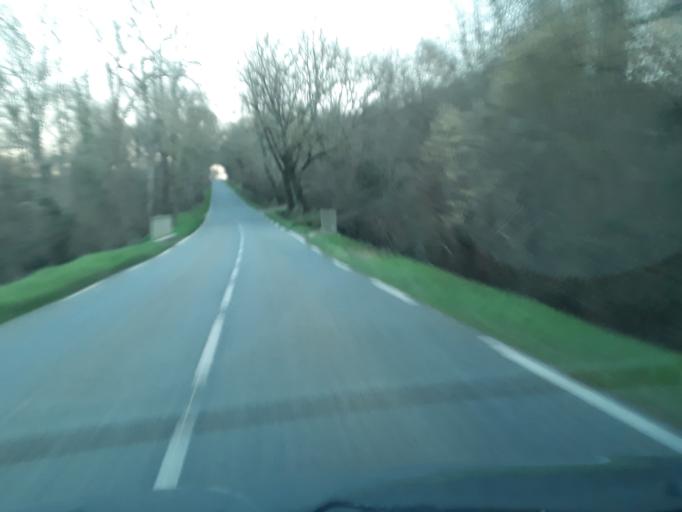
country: FR
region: Midi-Pyrenees
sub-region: Departement du Gers
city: Pujaudran
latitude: 43.5589
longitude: 1.1320
